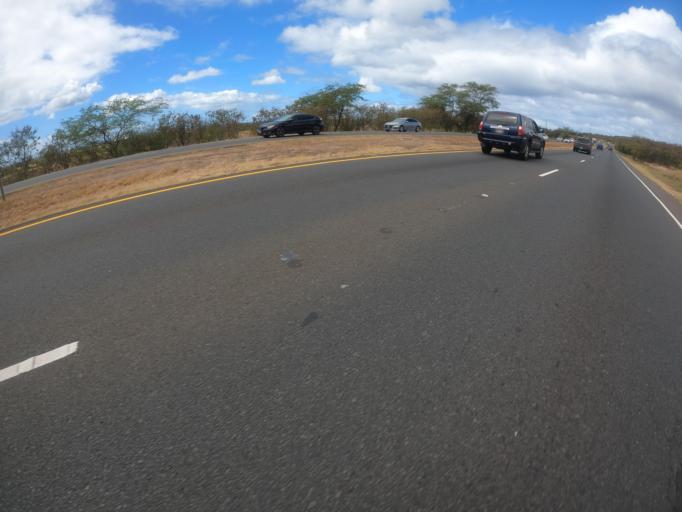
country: US
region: Hawaii
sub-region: Honolulu County
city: Makakilo City
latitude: 21.3385
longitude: -158.0993
